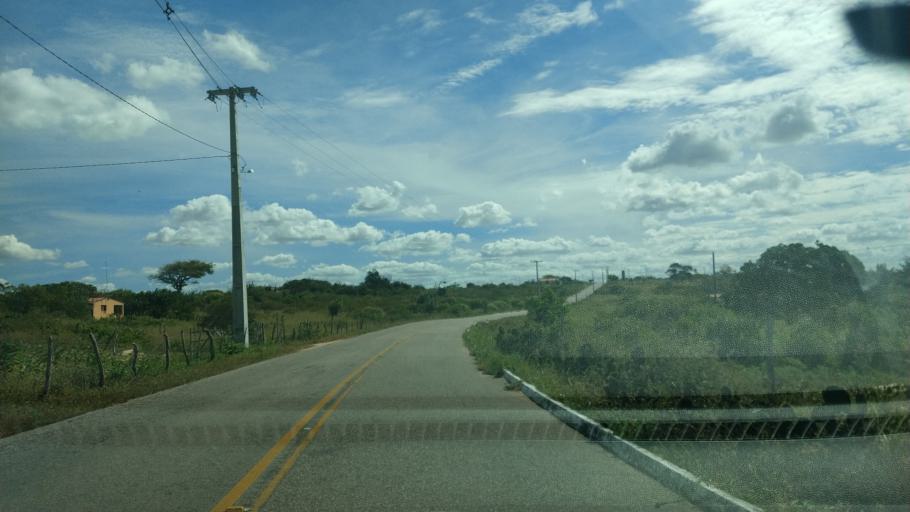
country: BR
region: Rio Grande do Norte
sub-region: Sao Jose Do Campestre
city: Sao Jose do Campestre
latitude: -6.4220
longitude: -35.7499
